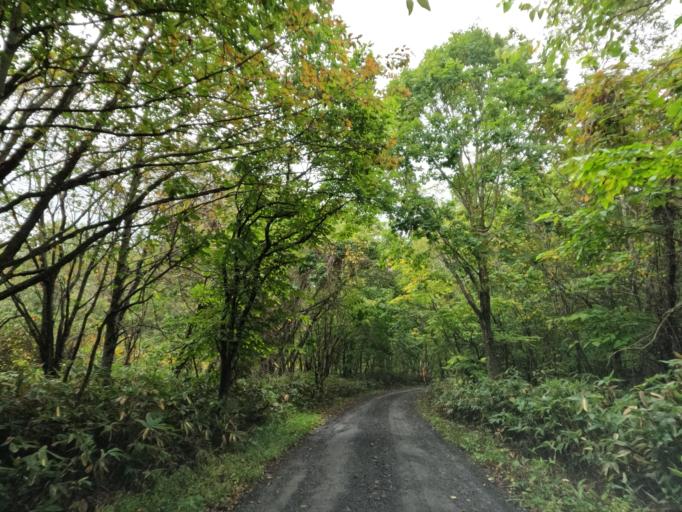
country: JP
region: Hokkaido
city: Date
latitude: 42.5010
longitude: 140.9212
